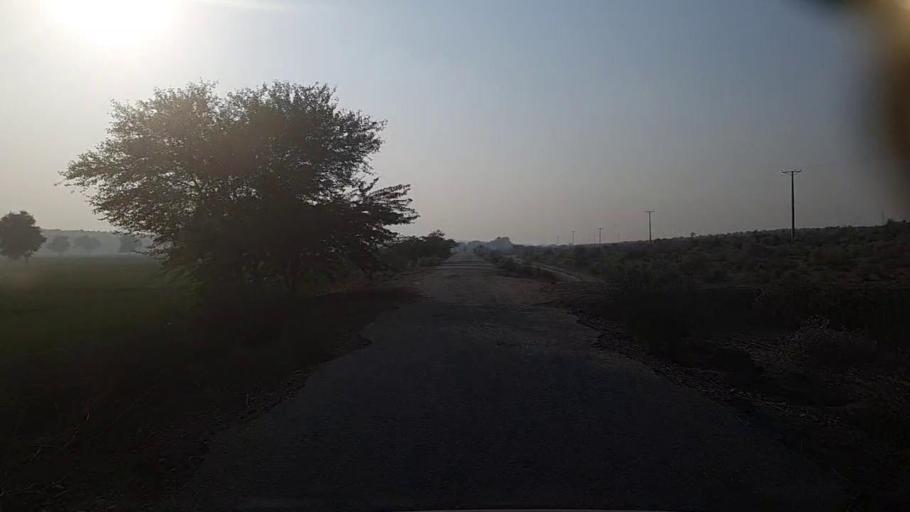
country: PK
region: Sindh
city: Pad Idan
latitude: 26.7140
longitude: 68.4790
